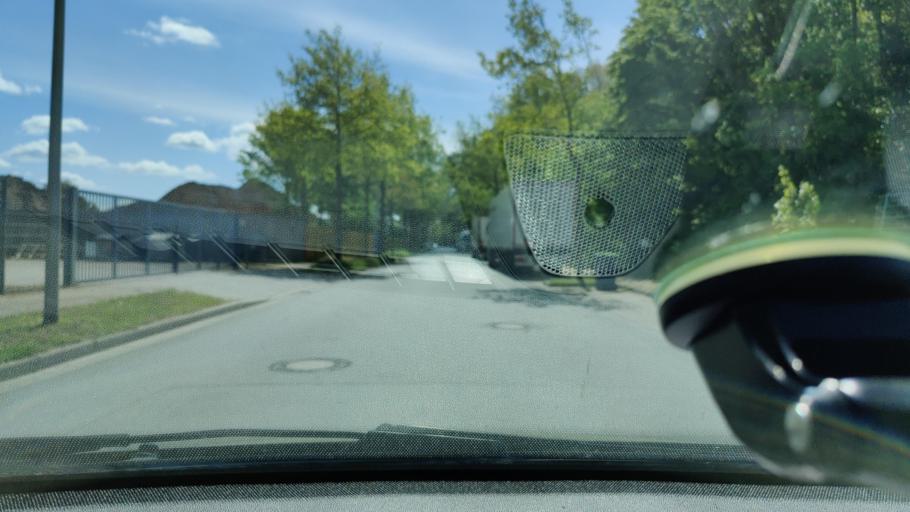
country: DE
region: North Rhine-Westphalia
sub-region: Regierungsbezirk Dusseldorf
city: Bocholt
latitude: 51.8108
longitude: 6.5511
